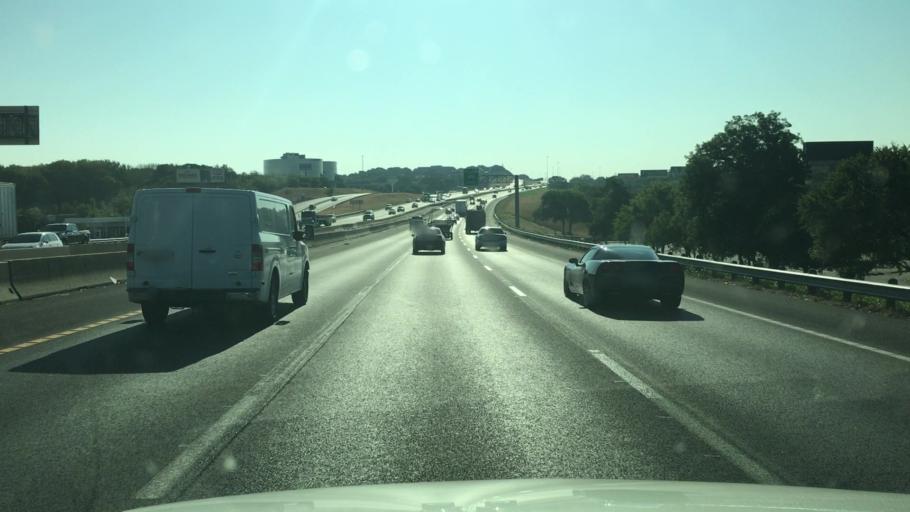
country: US
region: Texas
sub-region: Tarrant County
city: Haltom City
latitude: 32.7603
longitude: -97.2418
